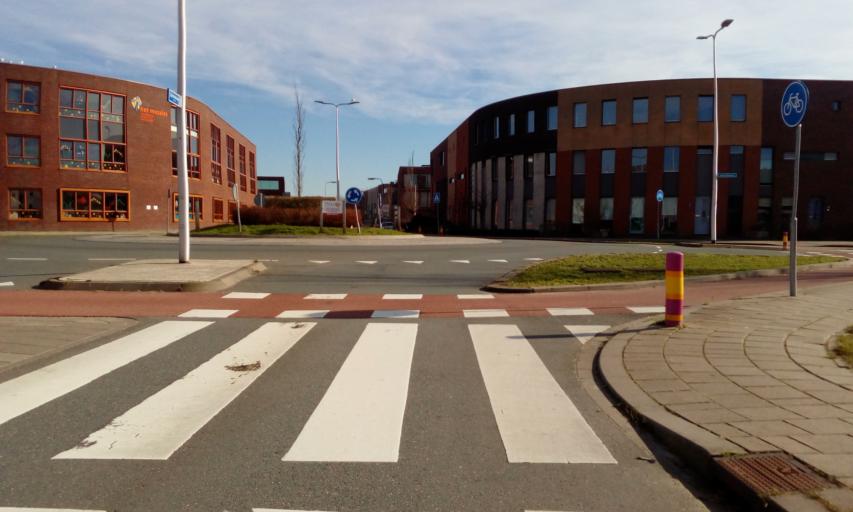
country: NL
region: South Holland
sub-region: Gemeente Alphen aan den Rijn
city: Alphen aan den Rijn
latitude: 52.1190
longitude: 4.6419
